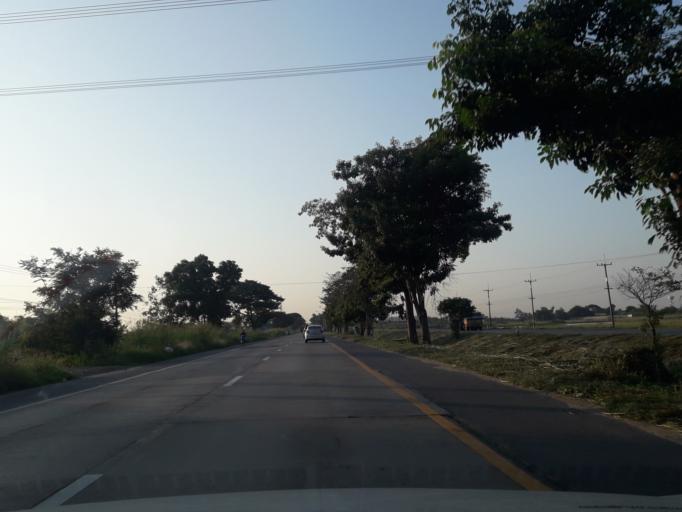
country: TH
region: Phra Nakhon Si Ayutthaya
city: Bang Pa-in
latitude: 14.2703
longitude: 100.5312
